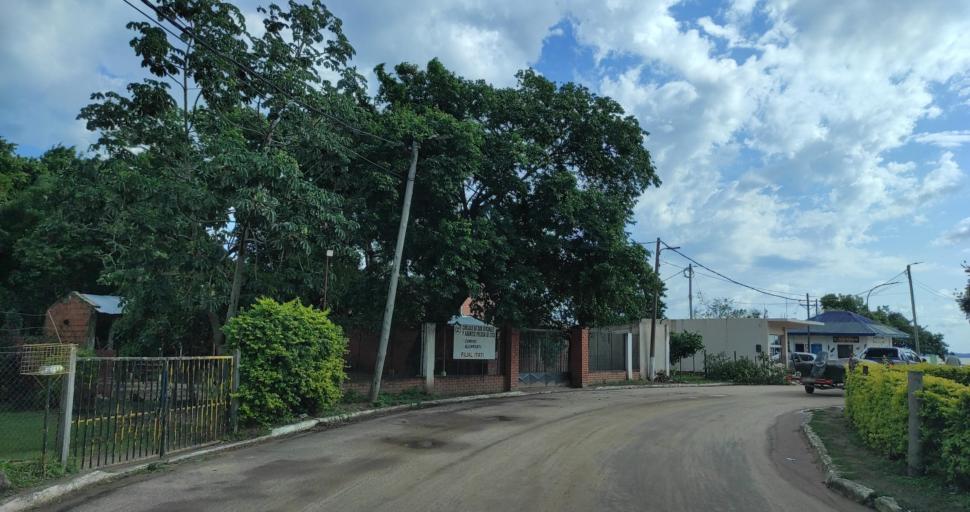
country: AR
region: Corrientes
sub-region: Departamento de Itati
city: Itati
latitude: -27.2674
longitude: -58.2475
